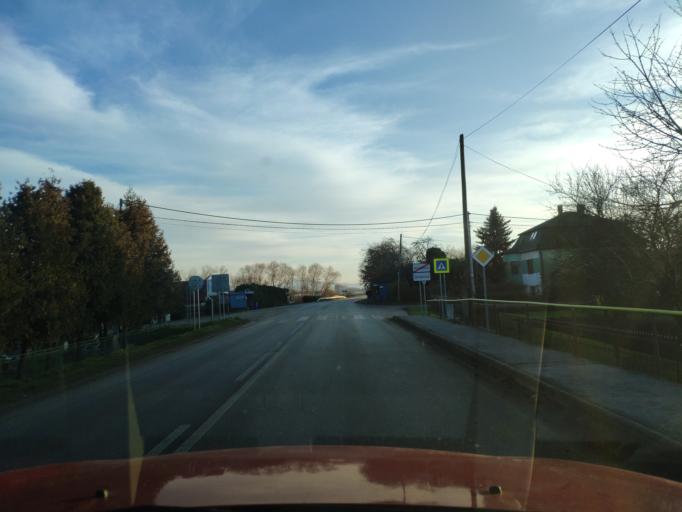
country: SK
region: Kosicky
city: Kosice
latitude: 48.8285
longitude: 21.2957
